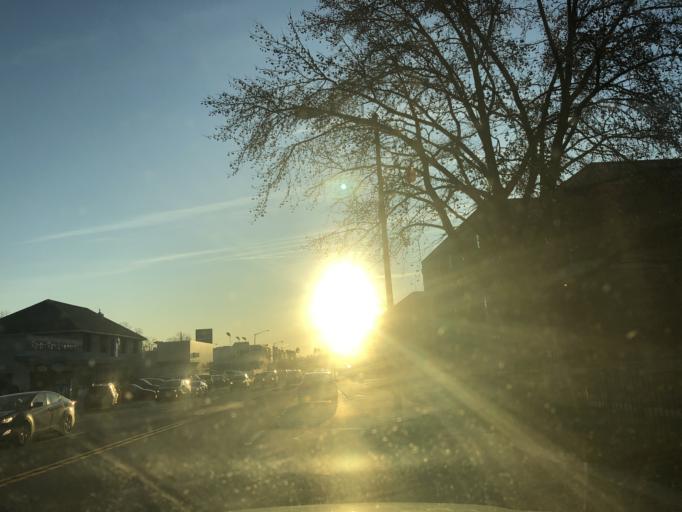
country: US
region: Pennsylvania
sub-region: Montgomery County
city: Ardmore
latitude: 40.0060
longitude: -75.2874
